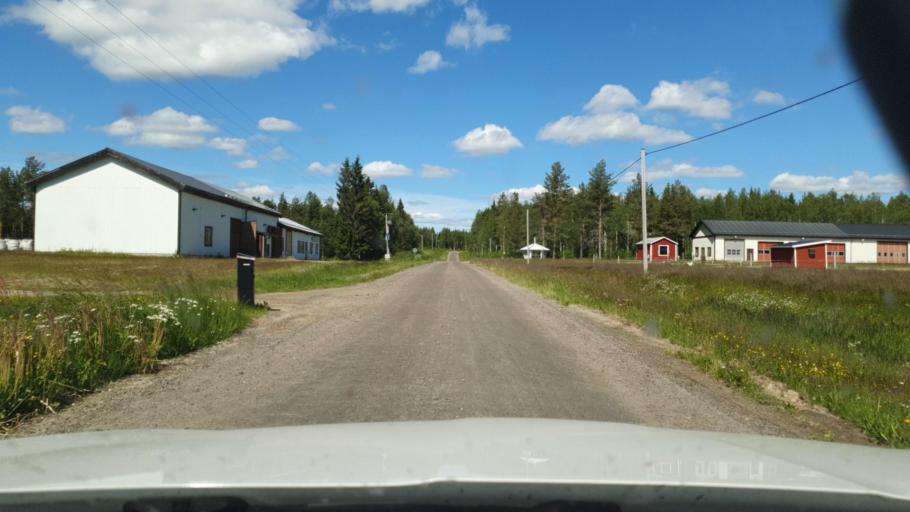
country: SE
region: Vaesterbotten
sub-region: Skelleftea Kommun
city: Backa
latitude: 65.1499
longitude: 21.1646
